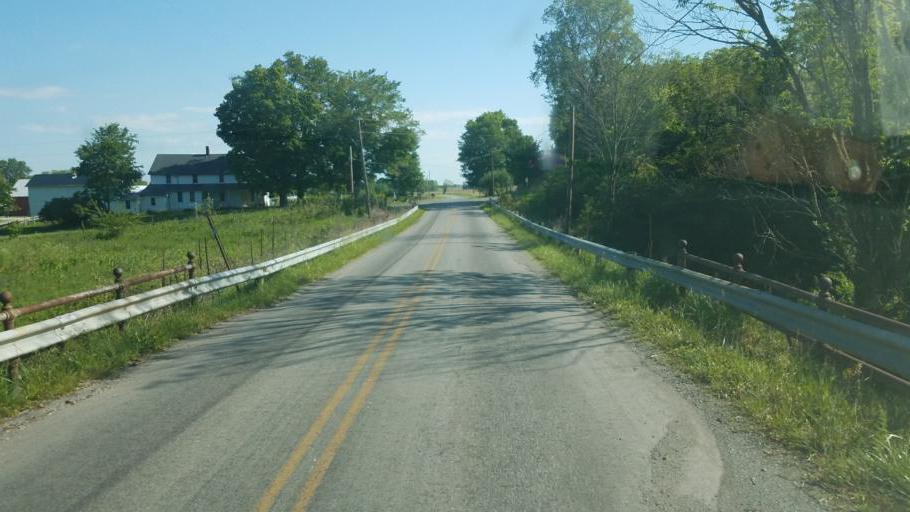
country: US
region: Ohio
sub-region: Hardin County
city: Kenton
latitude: 40.5930
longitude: -83.6176
